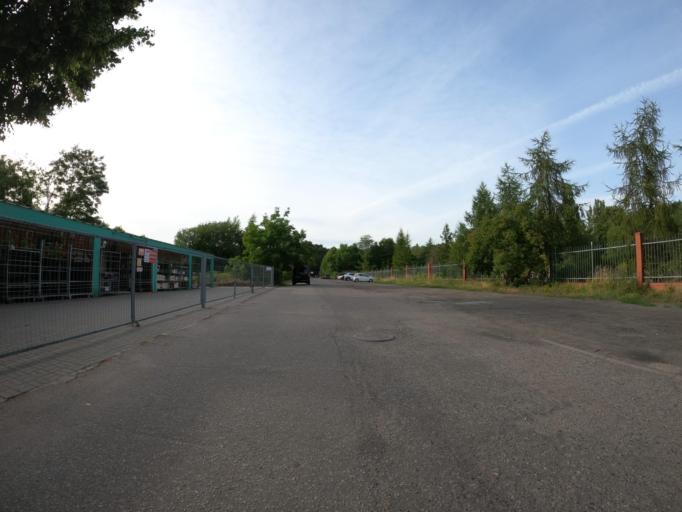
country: PL
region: West Pomeranian Voivodeship
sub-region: Szczecin
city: Szczecin
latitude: 53.4109
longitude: 14.5137
